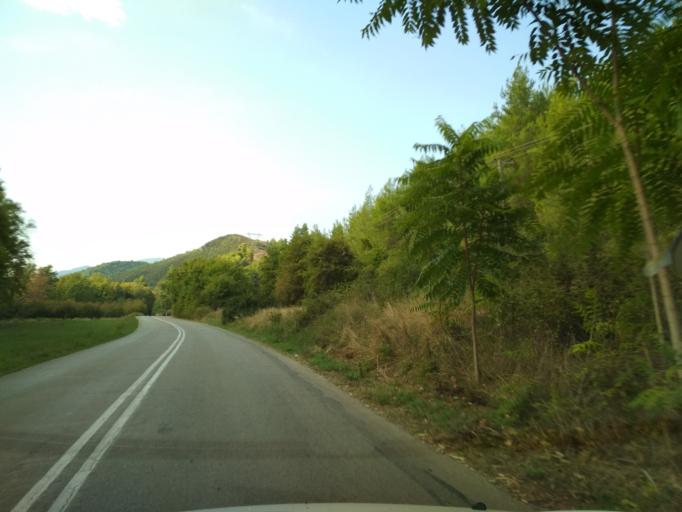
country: GR
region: Central Greece
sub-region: Nomos Evvoias
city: Mantoudi
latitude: 38.7818
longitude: 23.4702
